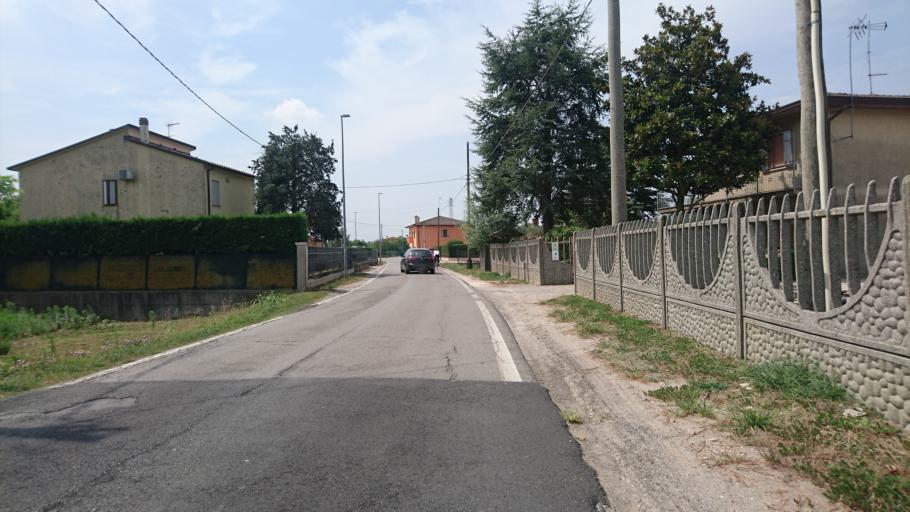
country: IT
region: Veneto
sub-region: Provincia di Rovigo
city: Rosolina
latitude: 45.0875
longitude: 12.2357
